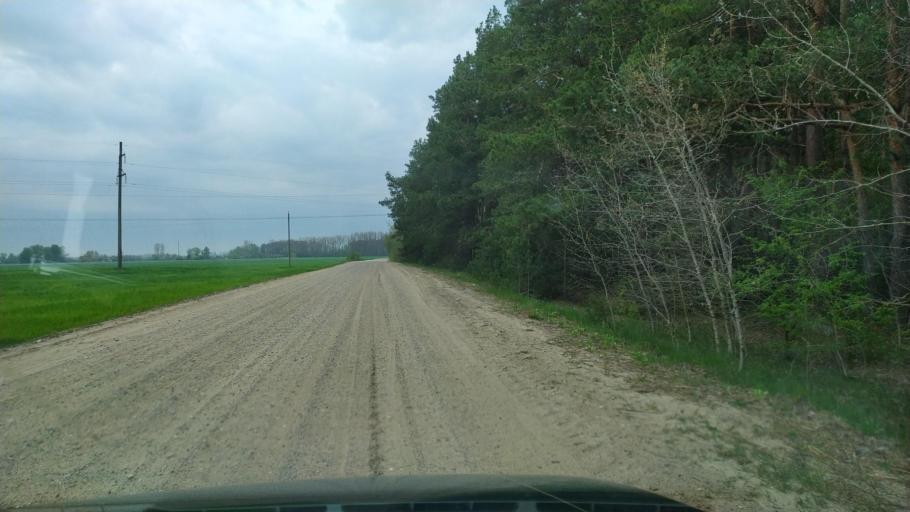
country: BY
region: Brest
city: Zhabinka
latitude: 52.1477
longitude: 24.0950
